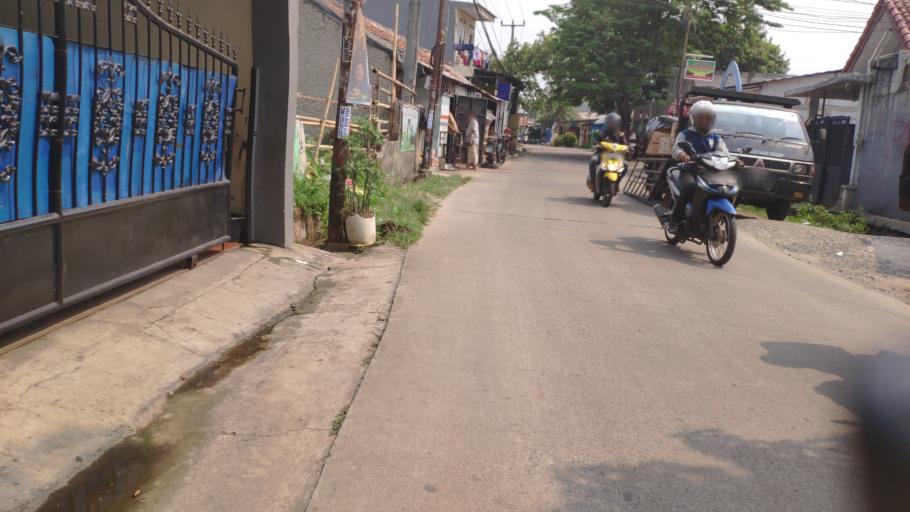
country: ID
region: West Java
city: Depok
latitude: -6.3854
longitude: 106.8047
